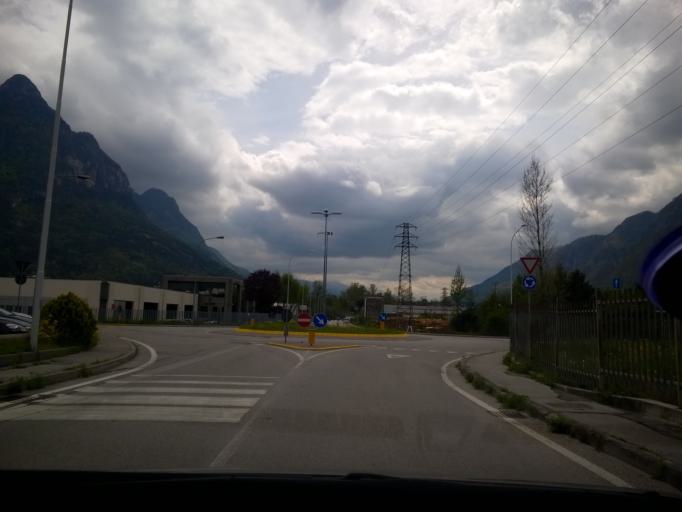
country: IT
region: Veneto
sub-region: Provincia di Belluno
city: Longarone
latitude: 46.2516
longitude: 12.3031
